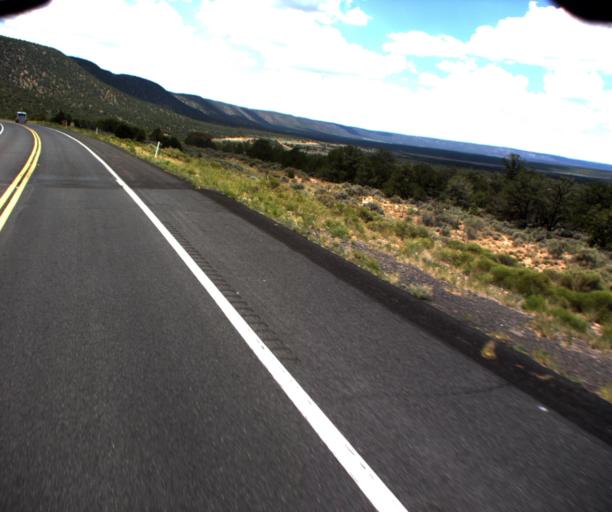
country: US
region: Arizona
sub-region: Coconino County
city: Grand Canyon
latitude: 35.9281
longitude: -111.7259
